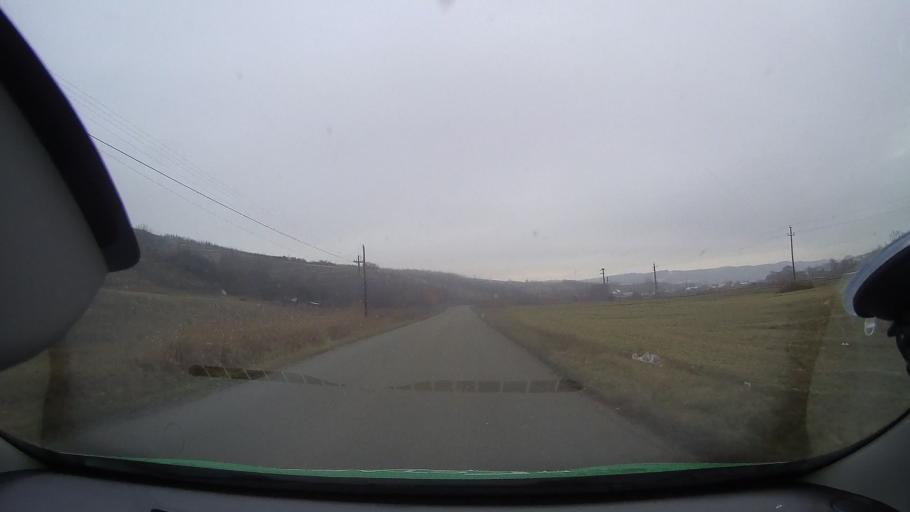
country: RO
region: Alba
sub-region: Comuna Farau
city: Farau
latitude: 46.3374
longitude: 23.9841
